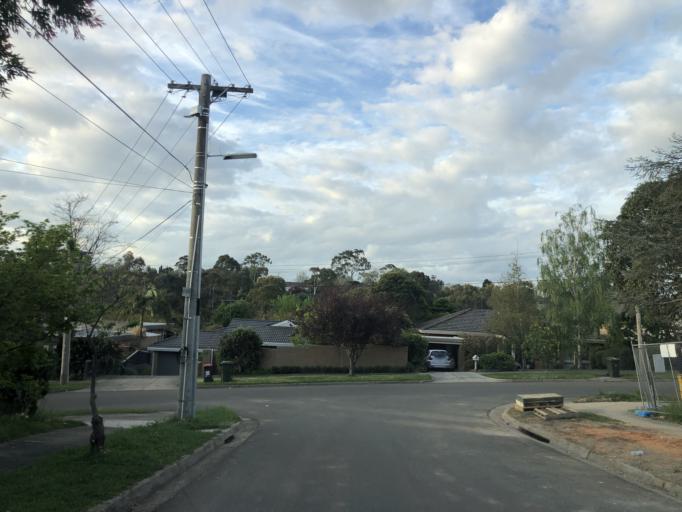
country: AU
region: Victoria
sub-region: Monash
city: Ashwood
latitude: -37.8710
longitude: 145.1280
